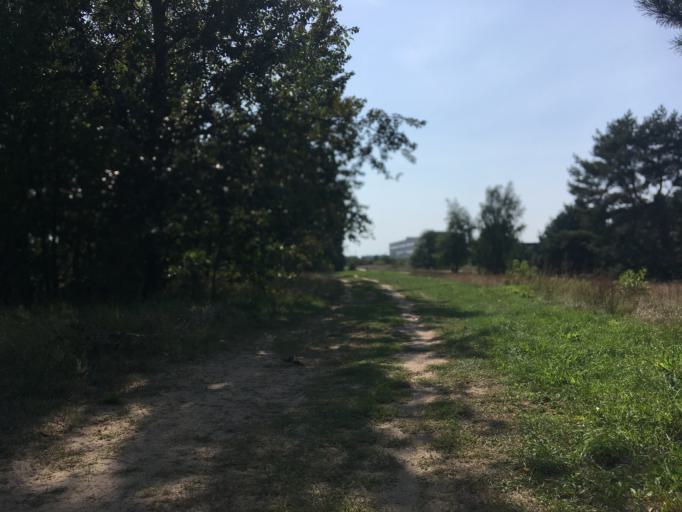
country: DE
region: Brandenburg
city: Erkner
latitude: 52.3997
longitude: 13.7240
